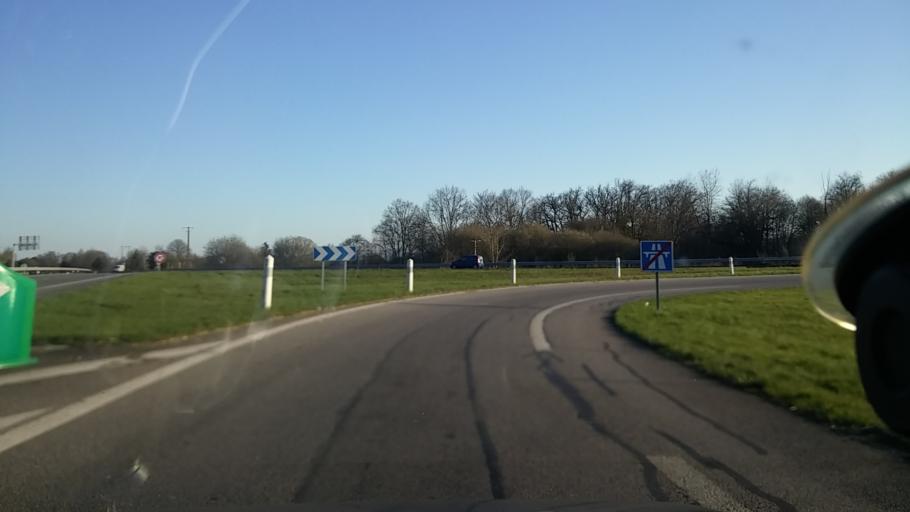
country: FR
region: Limousin
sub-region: Departement de la Haute-Vienne
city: Condat-sur-Vienne
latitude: 45.7804
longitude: 1.3045
